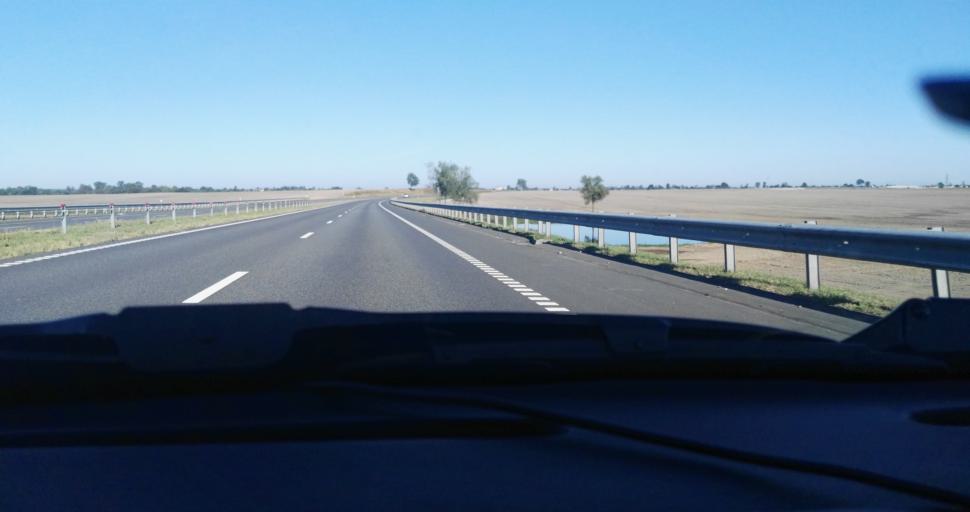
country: BY
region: Gomel
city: Buda-Kashalyova
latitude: 52.5063
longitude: 30.6401
